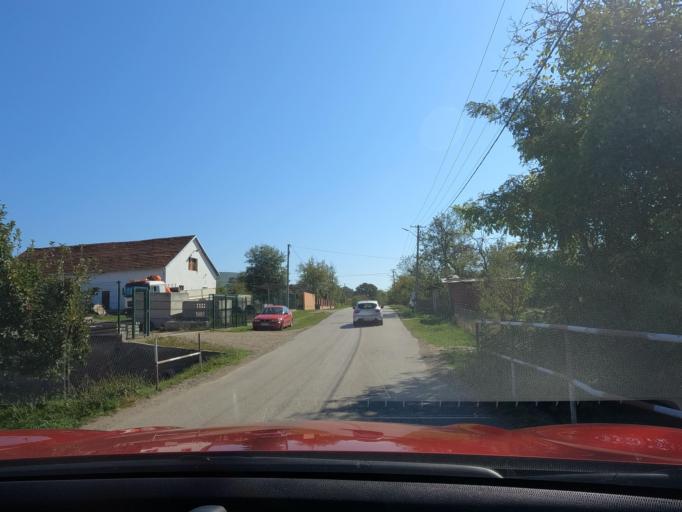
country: RS
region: Central Serbia
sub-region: Raski Okrug
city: Kraljevo
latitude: 43.7532
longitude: 20.6985
